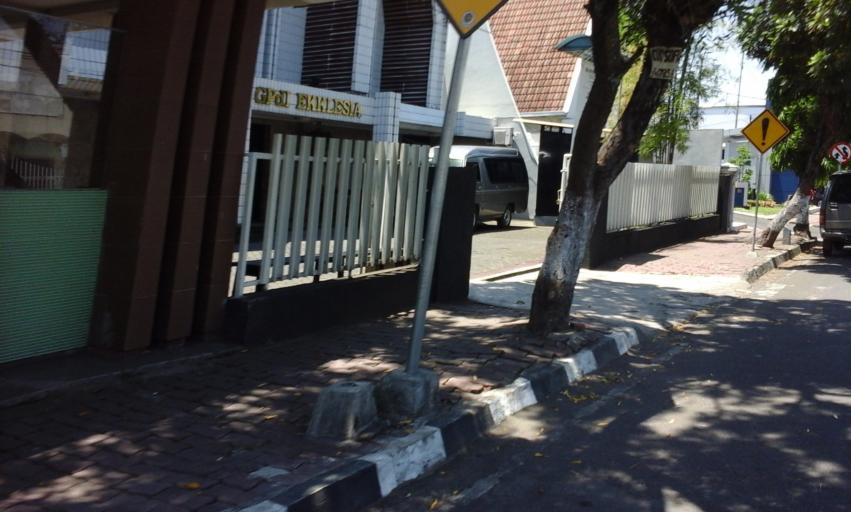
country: ID
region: East Java
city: Krajan
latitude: -8.1658
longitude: 113.7051
